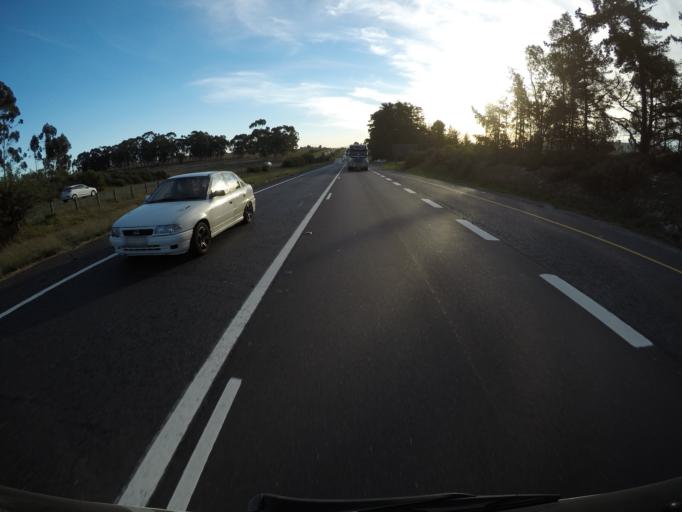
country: ZA
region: Western Cape
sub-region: City of Cape Town
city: Kraaifontein
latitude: -33.8214
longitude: 18.7856
